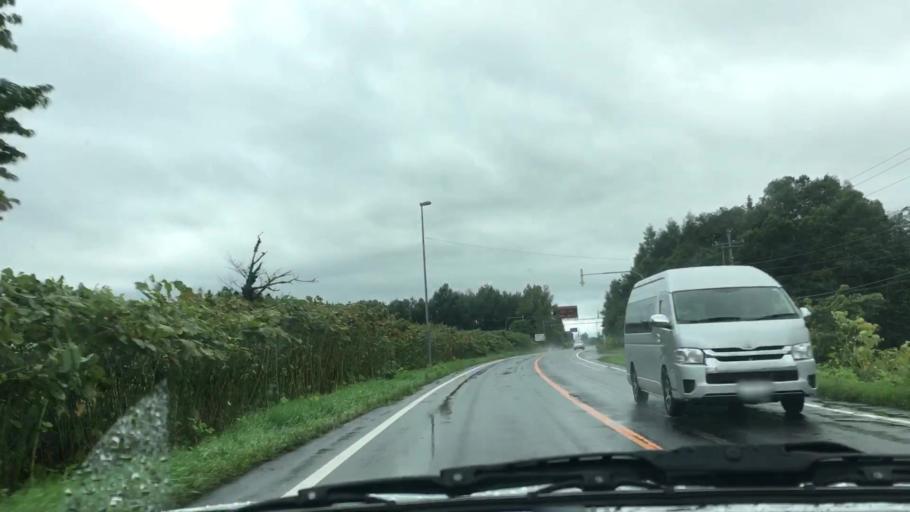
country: JP
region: Hokkaido
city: Niseko Town
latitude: 42.6980
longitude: 140.8441
